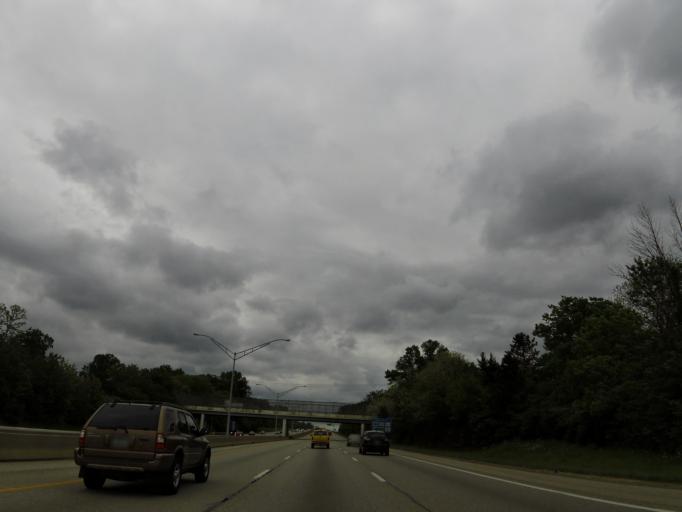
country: US
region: Ohio
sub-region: Hamilton County
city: Montgomery
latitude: 39.2274
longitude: -84.3665
